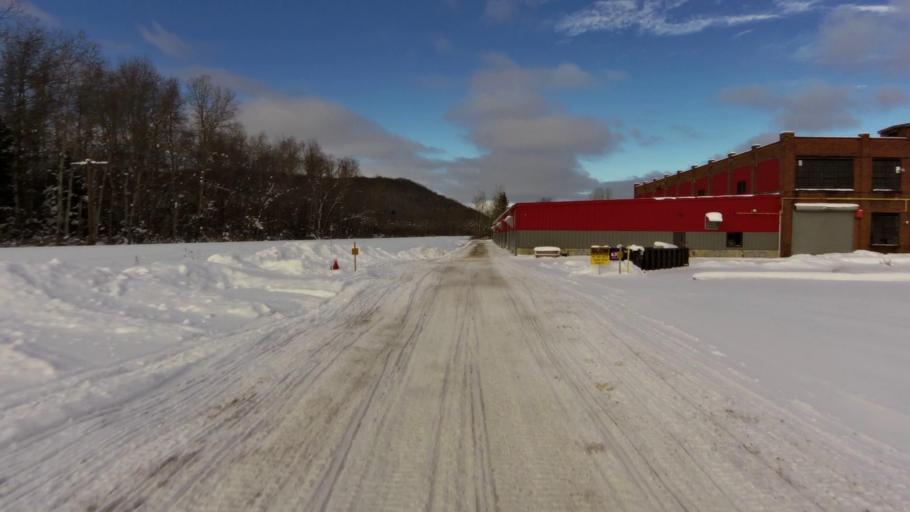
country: US
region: New York
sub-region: Cattaraugus County
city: Franklinville
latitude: 42.3387
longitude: -78.4613
